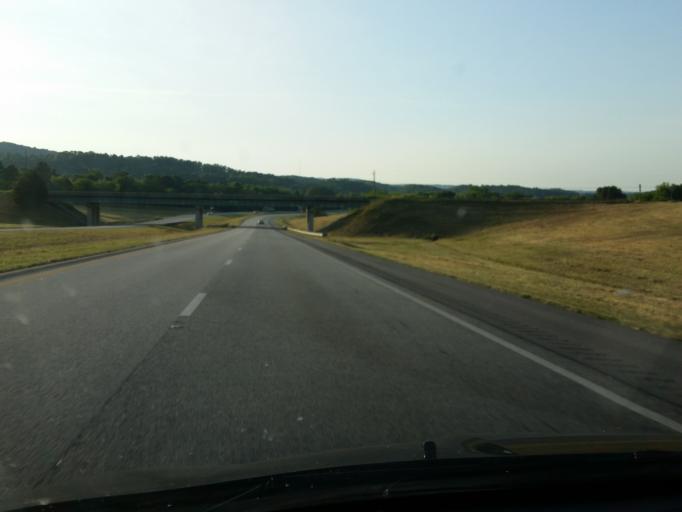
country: US
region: Georgia
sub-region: Dade County
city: Trenton
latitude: 34.7706
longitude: -85.5394
